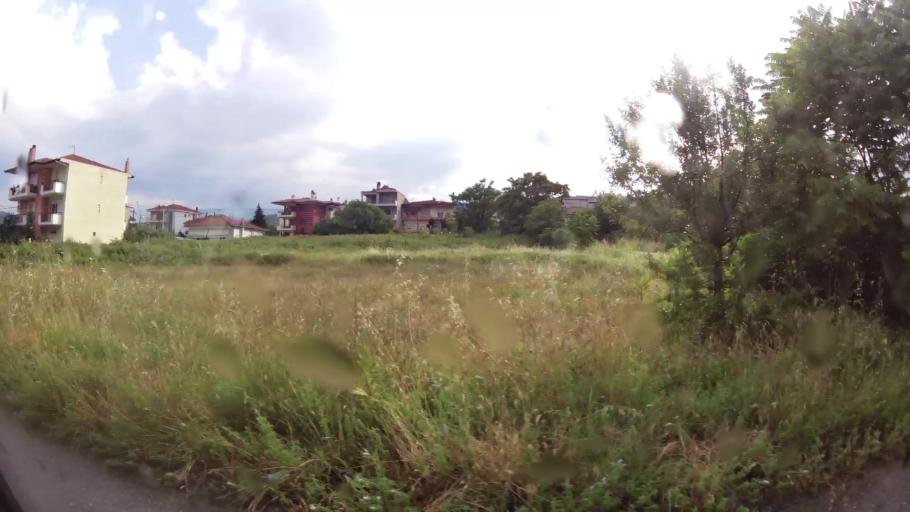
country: GR
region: Central Macedonia
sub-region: Nomos Imathias
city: Veroia
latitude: 40.5392
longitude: 22.2007
